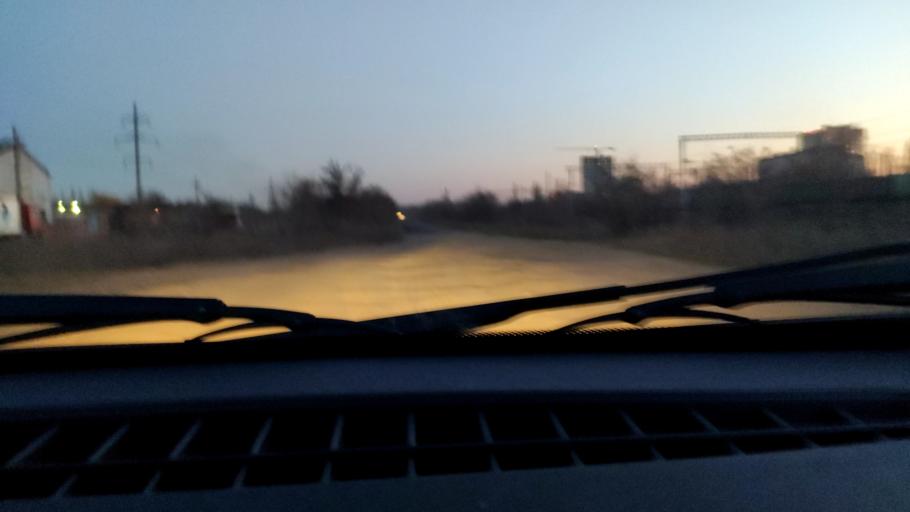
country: RU
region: Voronezj
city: Somovo
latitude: 51.7078
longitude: 39.2798
